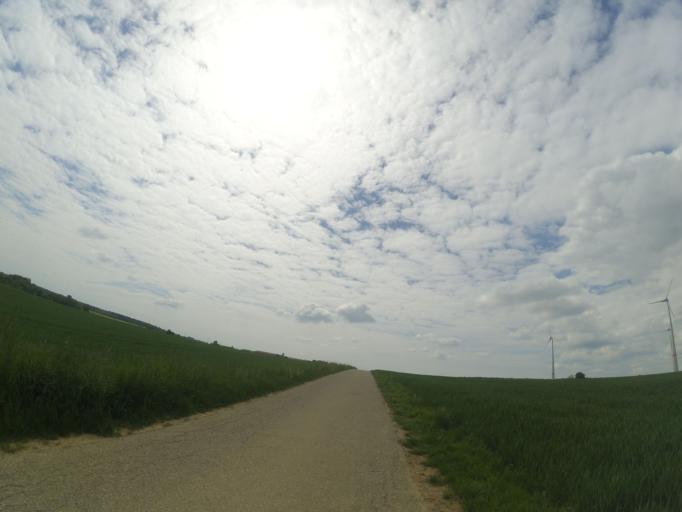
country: DE
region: Baden-Wuerttemberg
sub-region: Tuebingen Region
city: Berghulen
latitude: 48.4556
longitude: 9.7693
